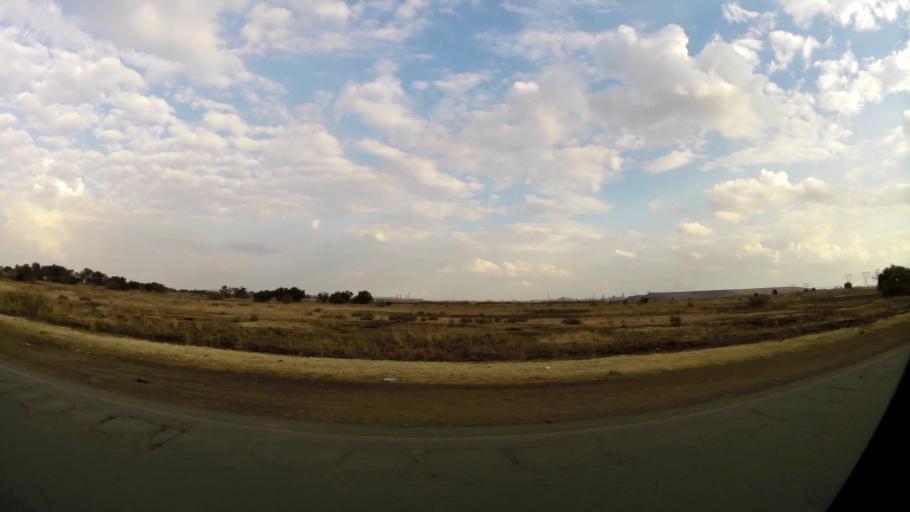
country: ZA
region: Gauteng
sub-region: Sedibeng District Municipality
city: Vanderbijlpark
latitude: -26.6189
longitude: 27.8319
